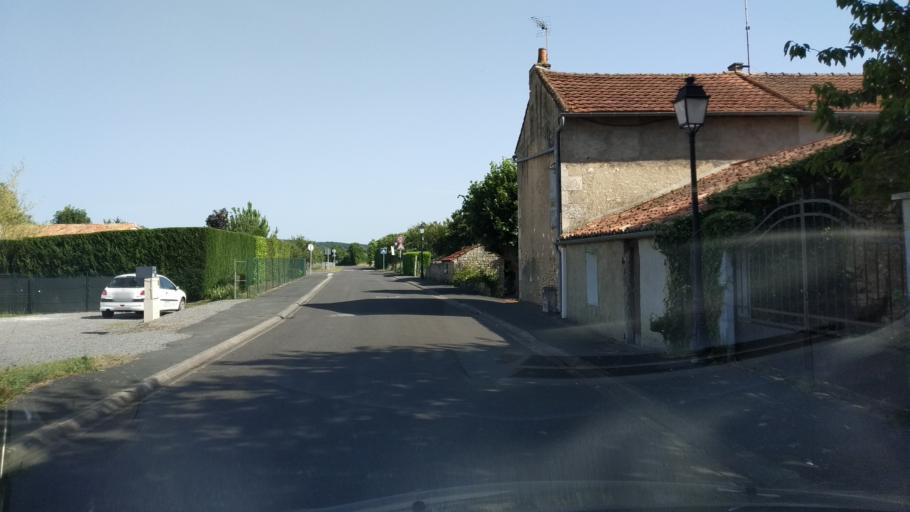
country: FR
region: Poitou-Charentes
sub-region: Departement de la Vienne
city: Lussac-les-Chateaux
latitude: 46.4419
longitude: 0.6681
